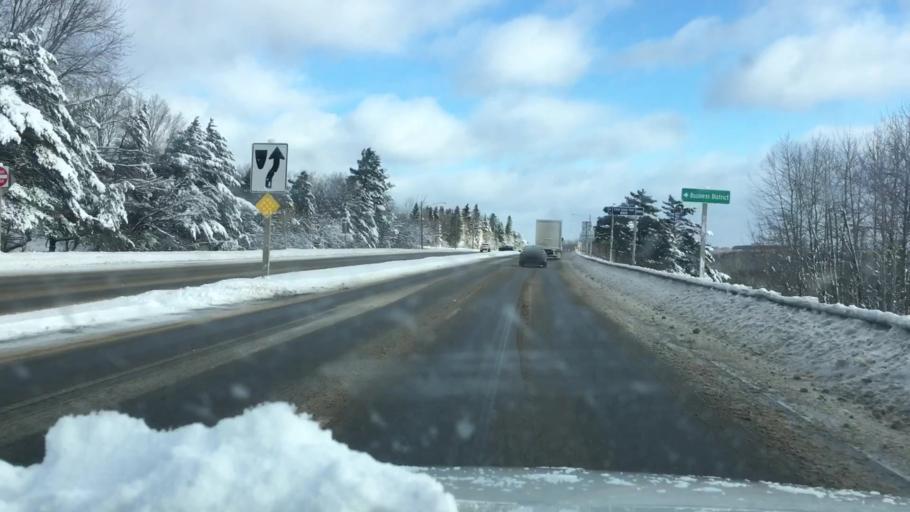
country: US
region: Maine
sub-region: Aroostook County
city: Caribou
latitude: 46.8595
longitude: -68.0041
